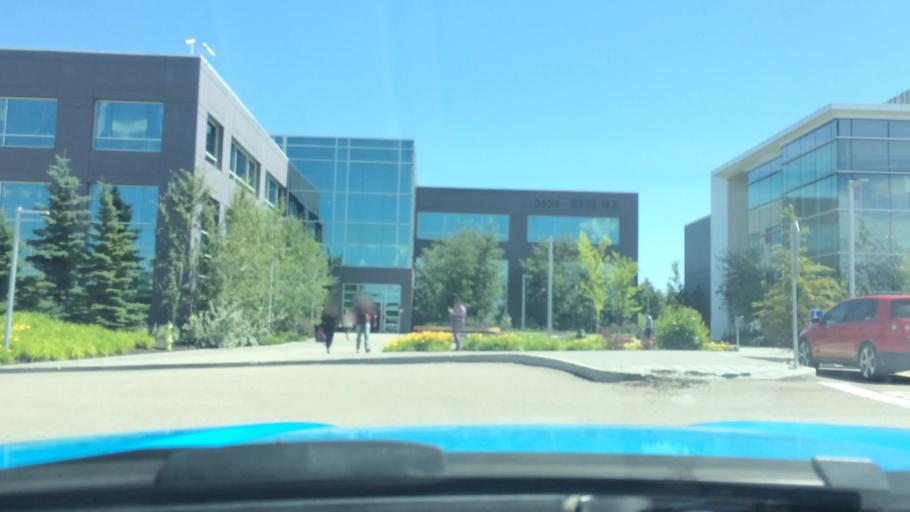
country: CA
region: Alberta
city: Calgary
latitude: 51.0850
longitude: -114.0039
